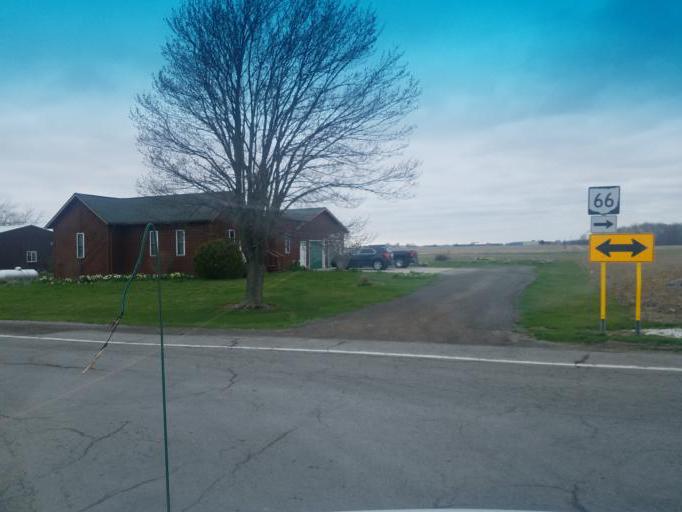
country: US
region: Ohio
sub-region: Allen County
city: Delphos
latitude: 40.9179
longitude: -84.3508
